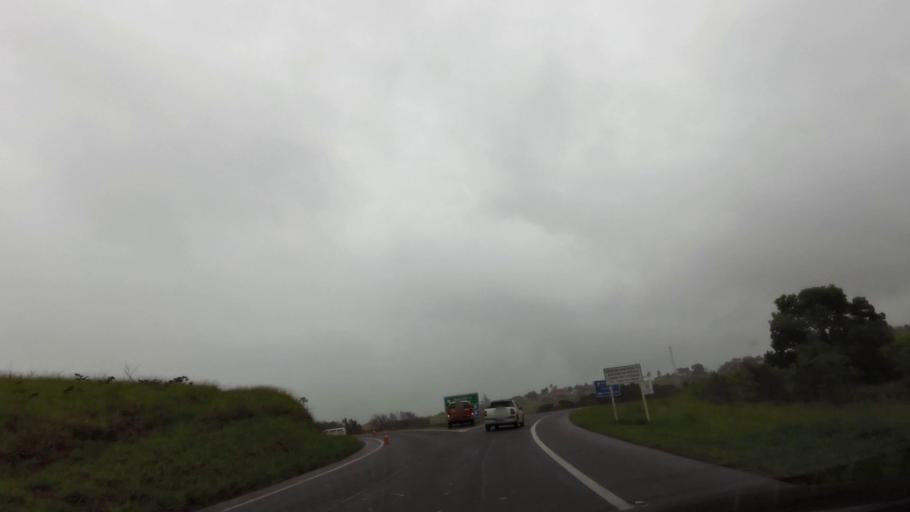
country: BR
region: Espirito Santo
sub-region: Guarapari
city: Guarapari
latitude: -20.7402
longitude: -40.5500
